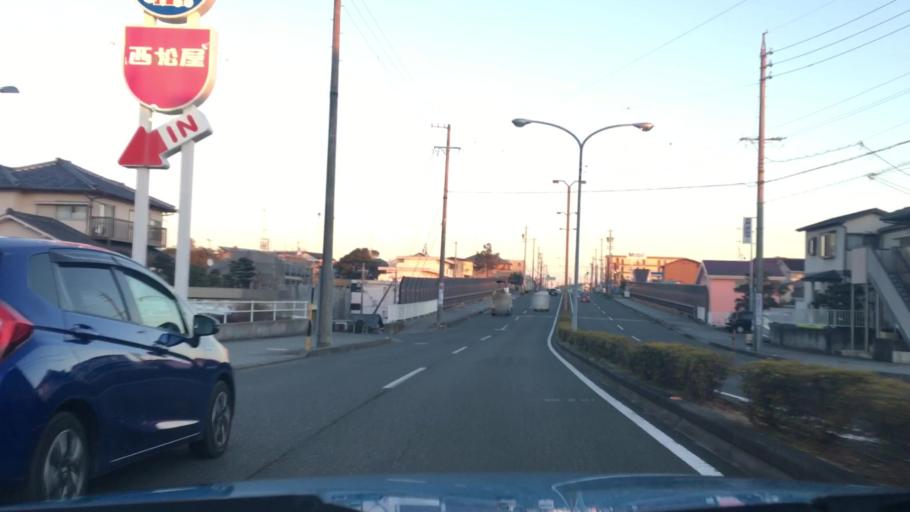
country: JP
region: Shizuoka
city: Hamamatsu
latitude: 34.7199
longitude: 137.7058
